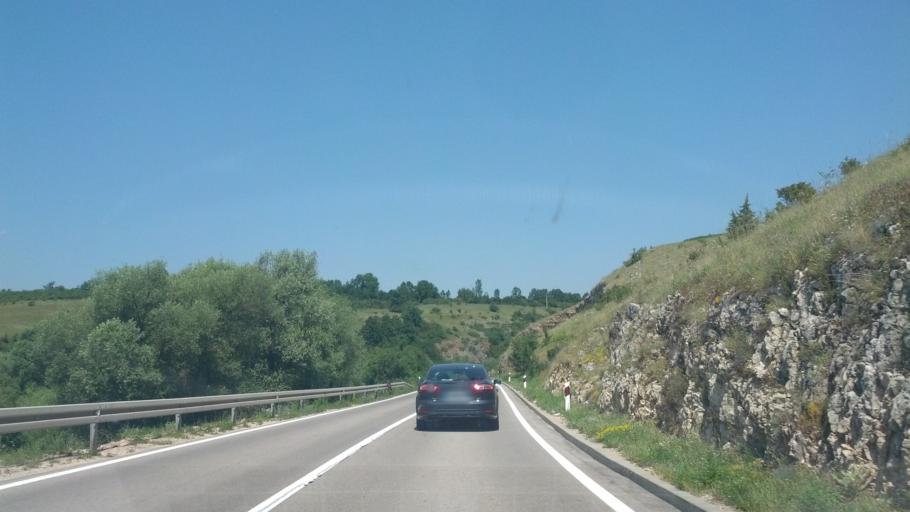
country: BA
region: Federation of Bosnia and Herzegovina
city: Izacic
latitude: 44.9180
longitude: 15.7137
